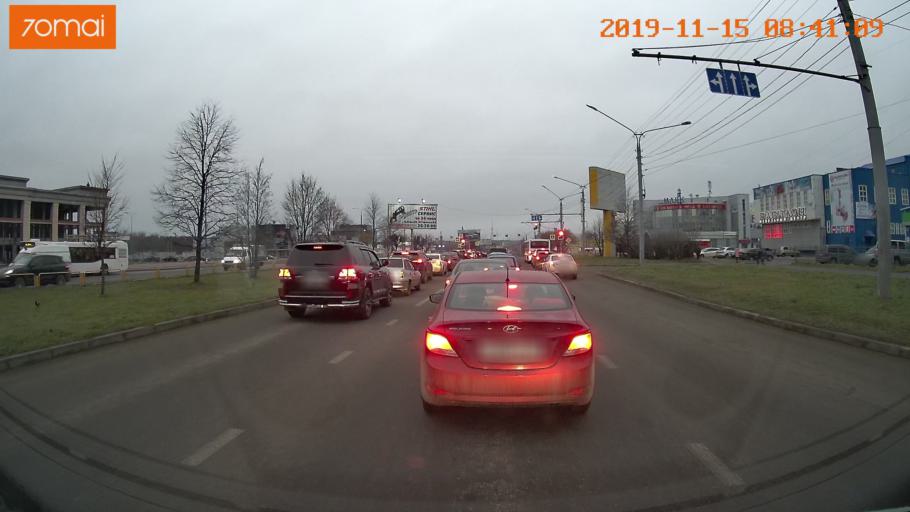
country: RU
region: Vologda
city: Cherepovets
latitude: 59.0974
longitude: 37.9119
